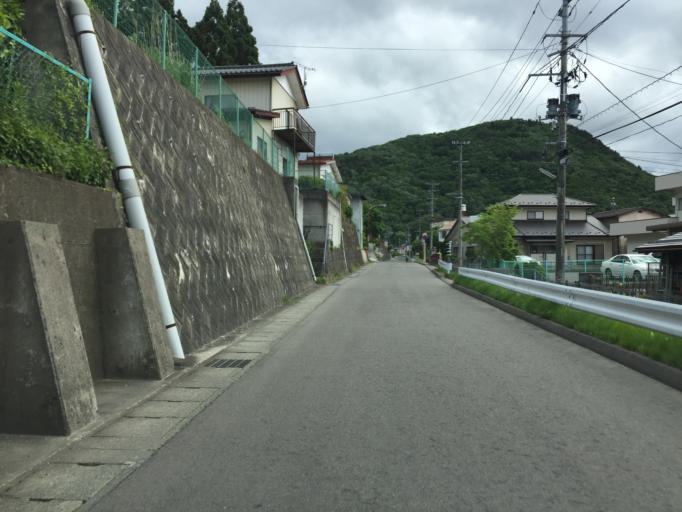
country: JP
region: Fukushima
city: Fukushima-shi
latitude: 37.7771
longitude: 140.4685
